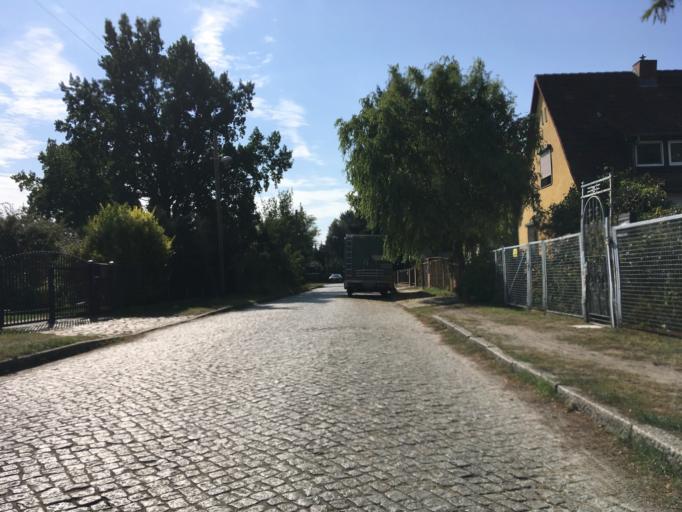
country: DE
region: Berlin
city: Mahlsdorf
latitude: 52.4925
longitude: 13.6046
